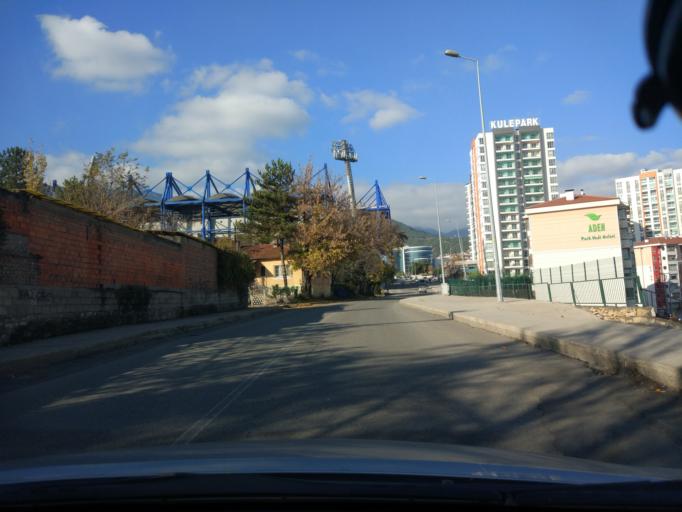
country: TR
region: Karabuk
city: Karabuk
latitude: 41.2029
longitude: 32.6217
